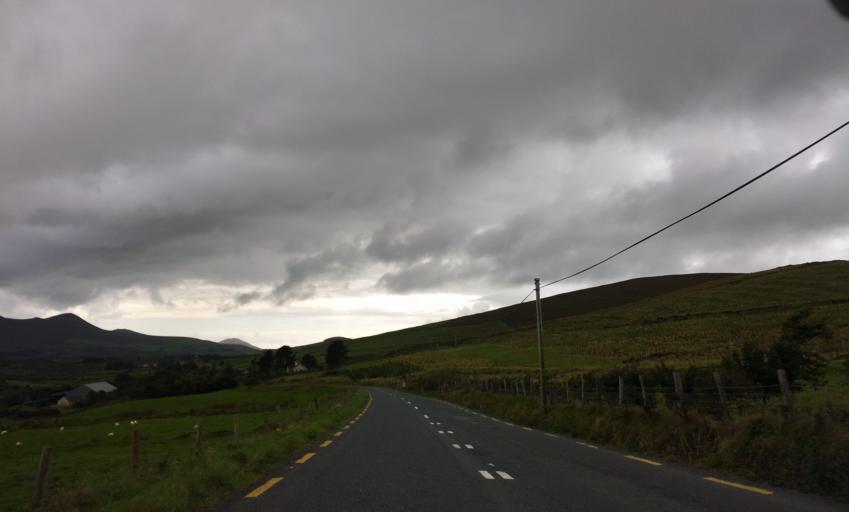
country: IE
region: Munster
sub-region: Ciarrai
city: Killorglin
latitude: 52.1957
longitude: -9.9366
